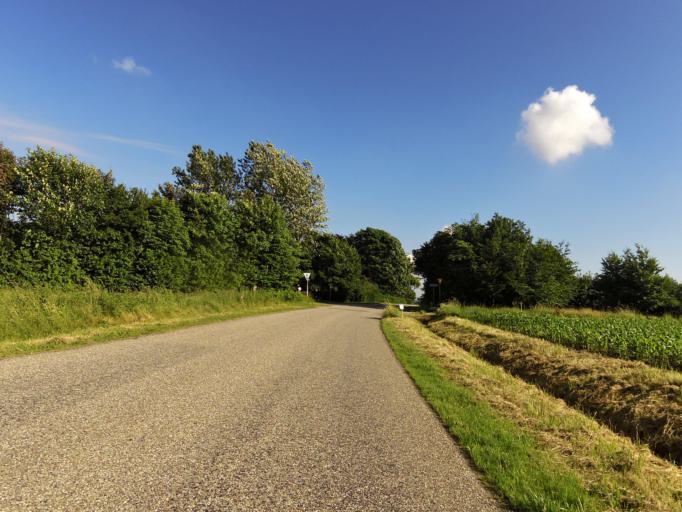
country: DK
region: South Denmark
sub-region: Vejen Kommune
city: Rodding
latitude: 55.3234
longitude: 9.1808
